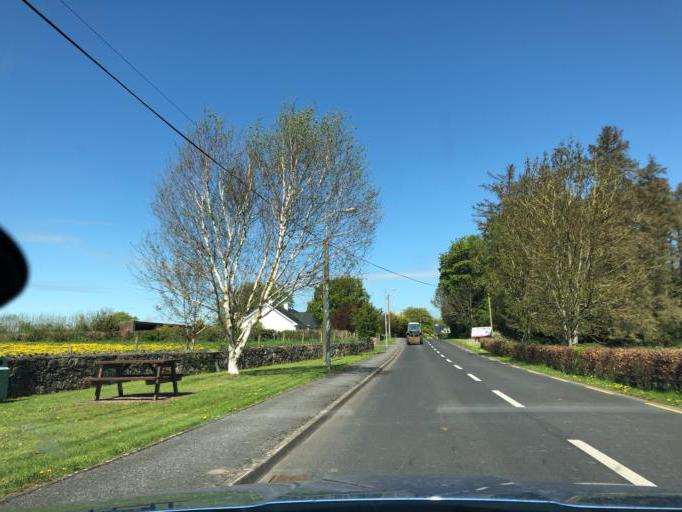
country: IE
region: Connaught
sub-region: County Galway
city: Portumna
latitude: 53.1455
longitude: -8.3699
